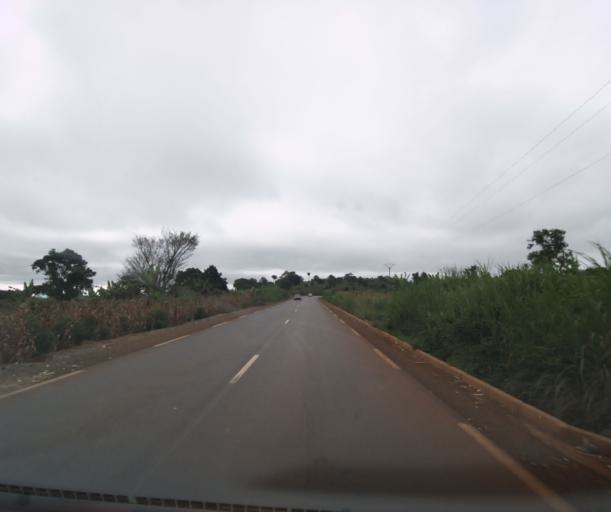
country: CM
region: West
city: Mbouda
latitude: 5.5525
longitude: 10.3245
